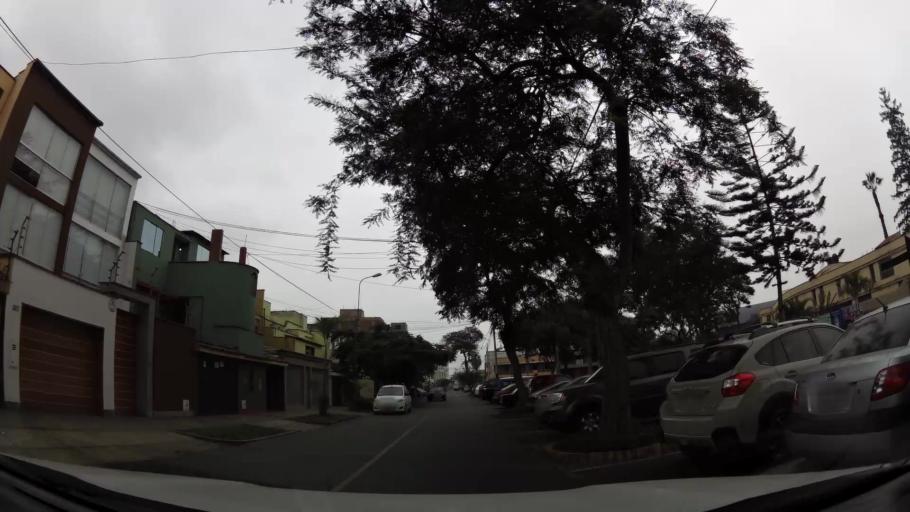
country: PE
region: Lima
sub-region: Lima
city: Surco
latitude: -12.1277
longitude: -76.9954
